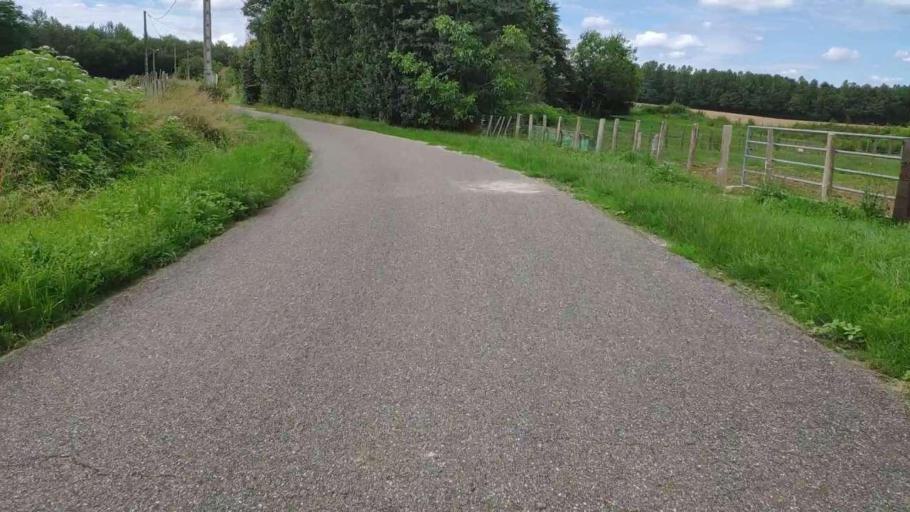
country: FR
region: Franche-Comte
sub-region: Departement du Jura
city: Chaussin
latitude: 46.8867
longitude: 5.4476
